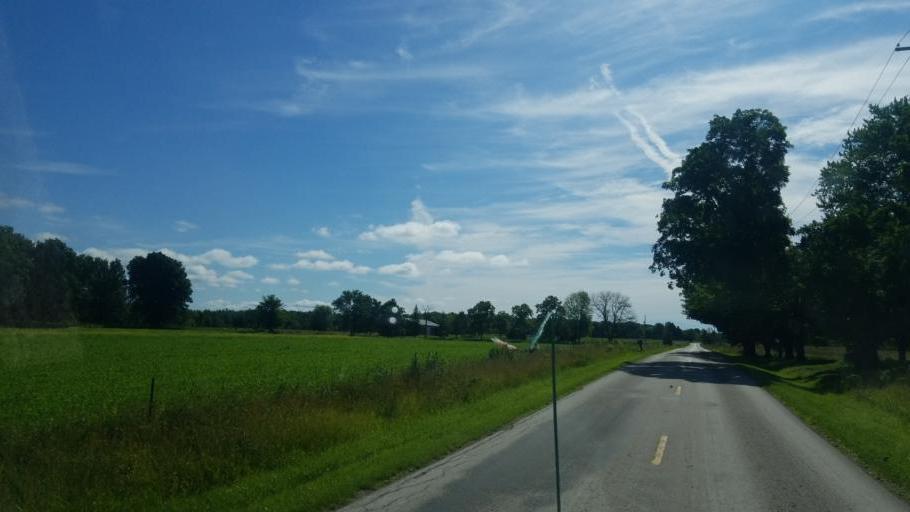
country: US
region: Ohio
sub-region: Ashtabula County
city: North Kingsville
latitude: 41.7819
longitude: -80.5794
